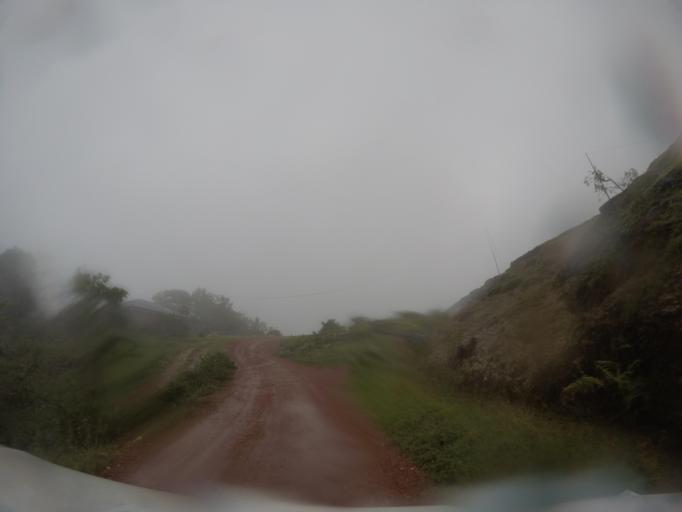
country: TL
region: Baucau
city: Venilale
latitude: -8.6394
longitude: 126.4167
